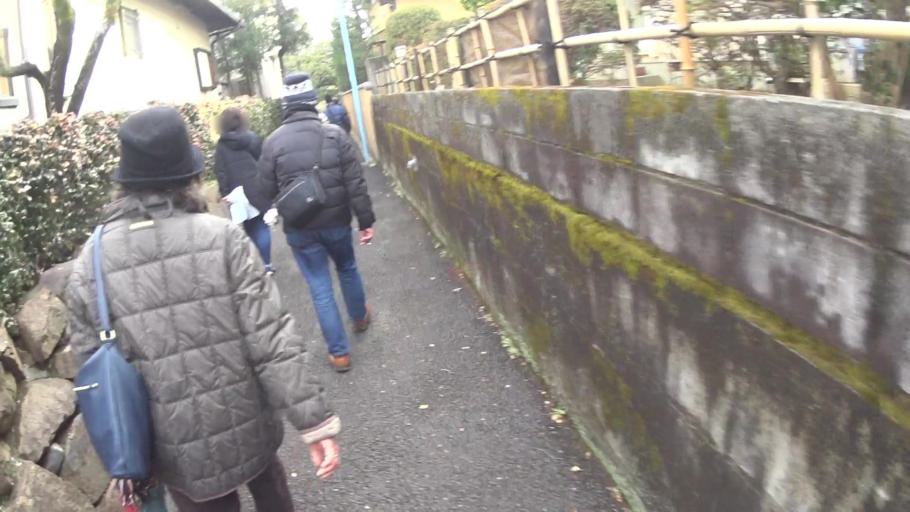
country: JP
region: Tokyo
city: Musashino
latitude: 35.7176
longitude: 139.5882
